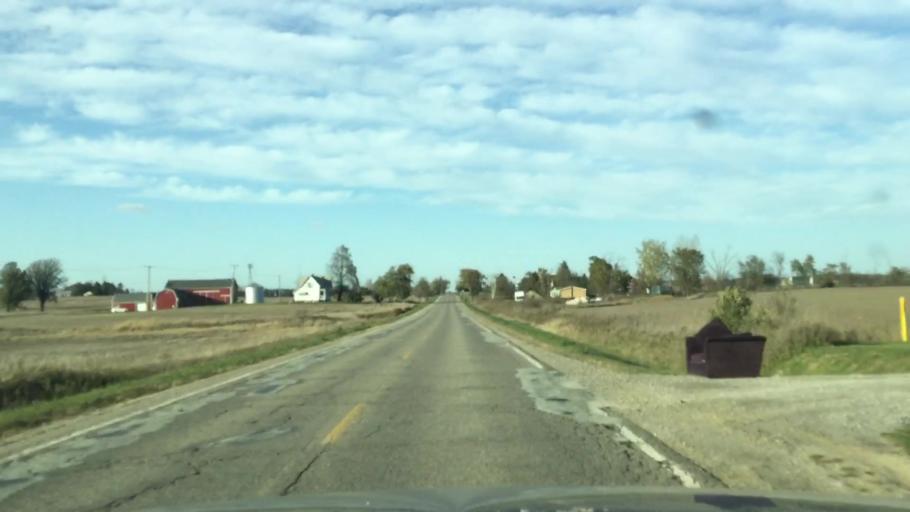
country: US
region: Michigan
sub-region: Lapeer County
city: North Branch
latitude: 43.2532
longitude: -83.1977
